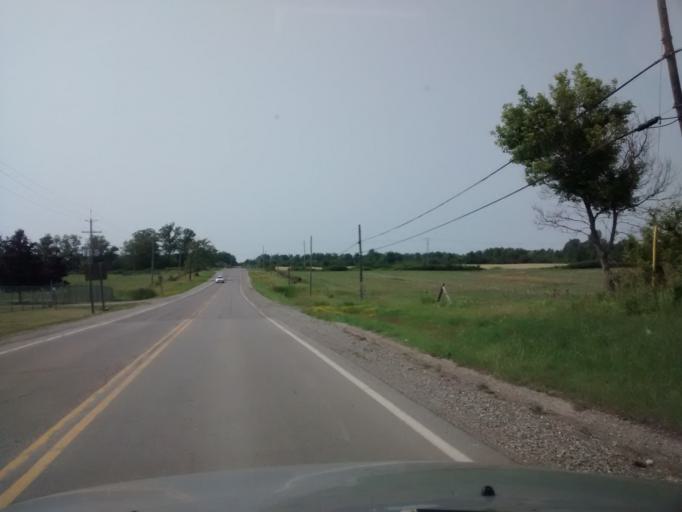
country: CA
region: Ontario
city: Ancaster
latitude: 42.9648
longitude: -79.8647
